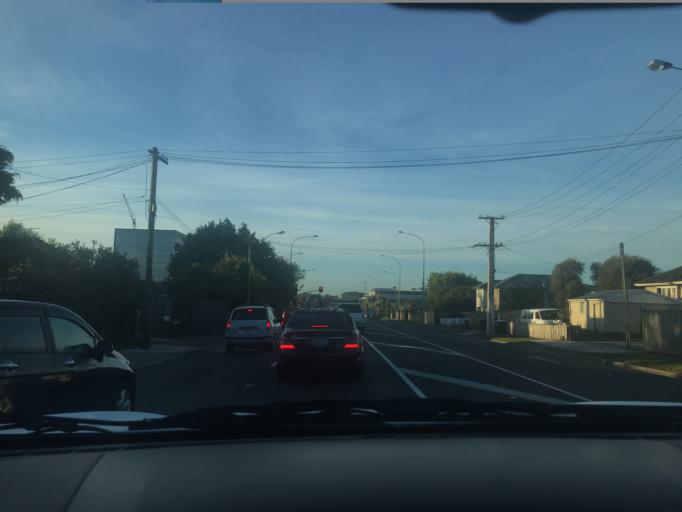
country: NZ
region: Auckland
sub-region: Auckland
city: Tamaki
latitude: -36.9121
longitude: 174.8382
